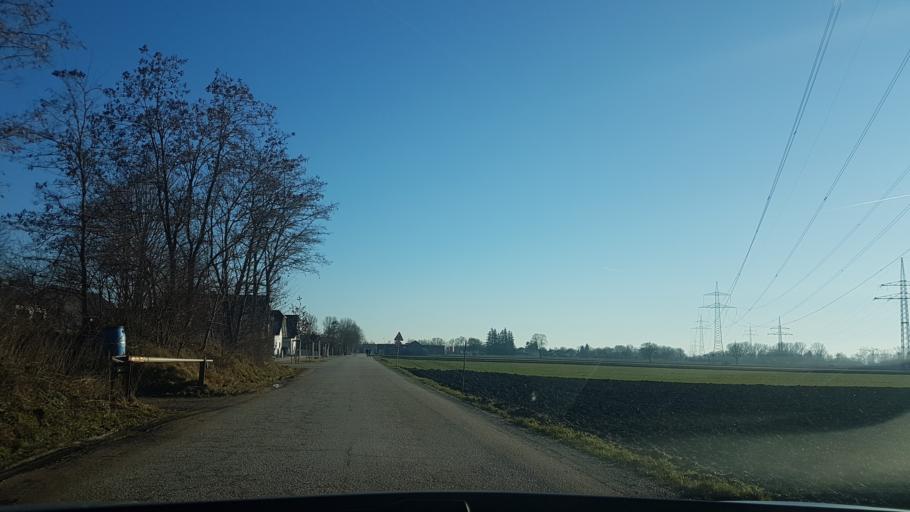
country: DE
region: Bavaria
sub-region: Upper Bavaria
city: Moosinning
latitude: 48.2803
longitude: 11.8240
